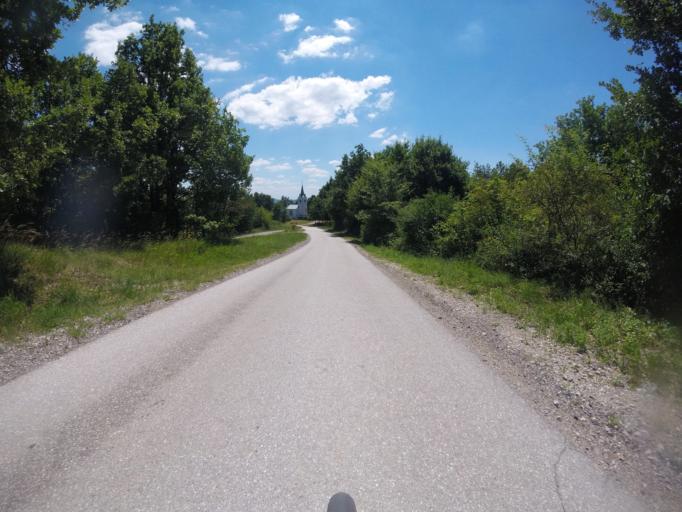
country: SI
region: Metlika
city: Metlika
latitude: 45.6973
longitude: 15.3869
